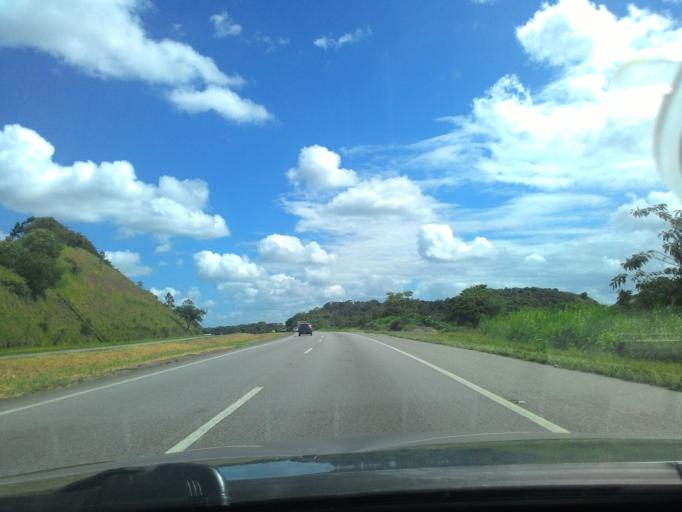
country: BR
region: Sao Paulo
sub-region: Registro
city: Registro
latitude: -24.5772
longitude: -47.8845
